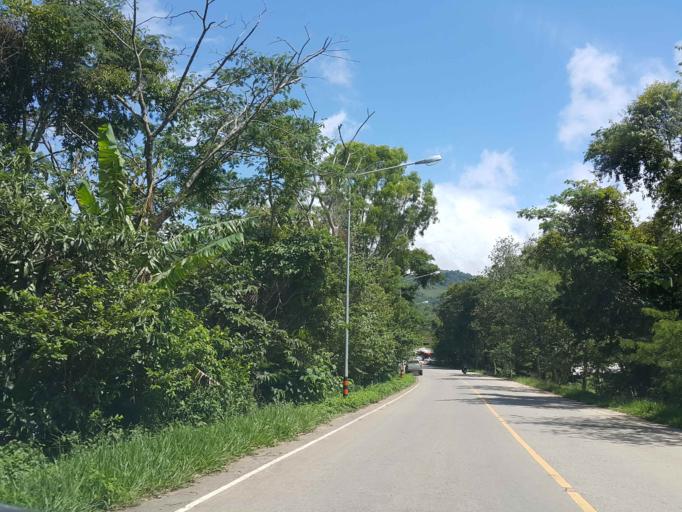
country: TH
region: Chiang Mai
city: Mae Chaem
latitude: 18.5329
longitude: 98.5218
